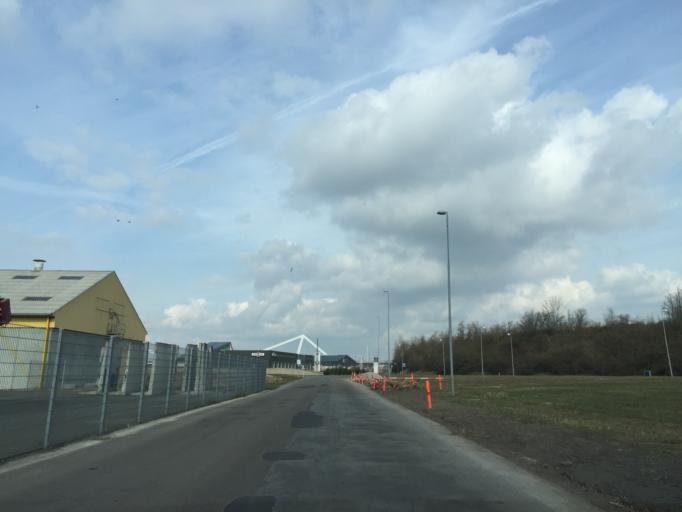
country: DK
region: South Denmark
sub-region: Odense Kommune
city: Odense
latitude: 55.4185
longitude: 10.3808
